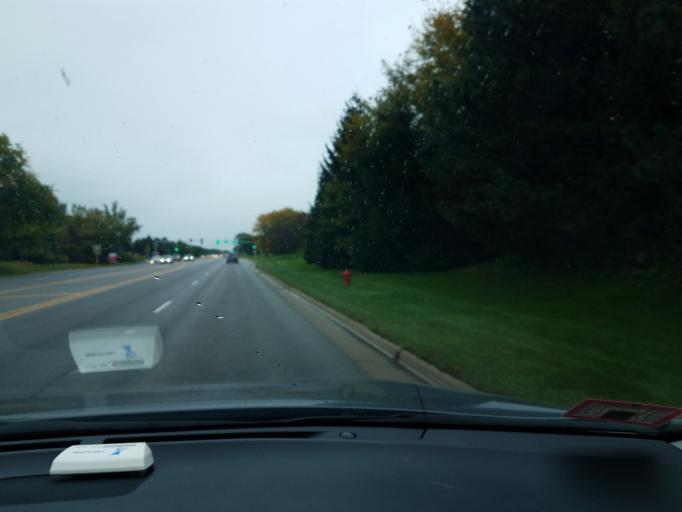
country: US
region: Illinois
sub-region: Lake County
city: Lincolnshire
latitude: 42.1902
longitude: -87.9292
